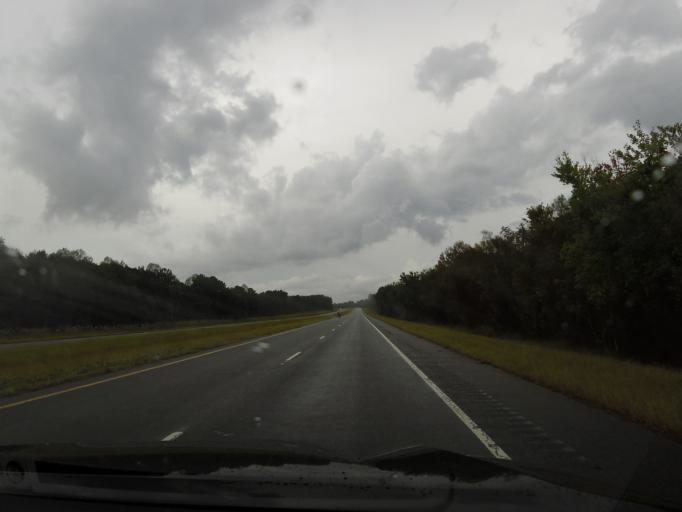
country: US
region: Georgia
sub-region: McIntosh County
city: Darien
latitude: 31.4190
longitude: -81.6646
